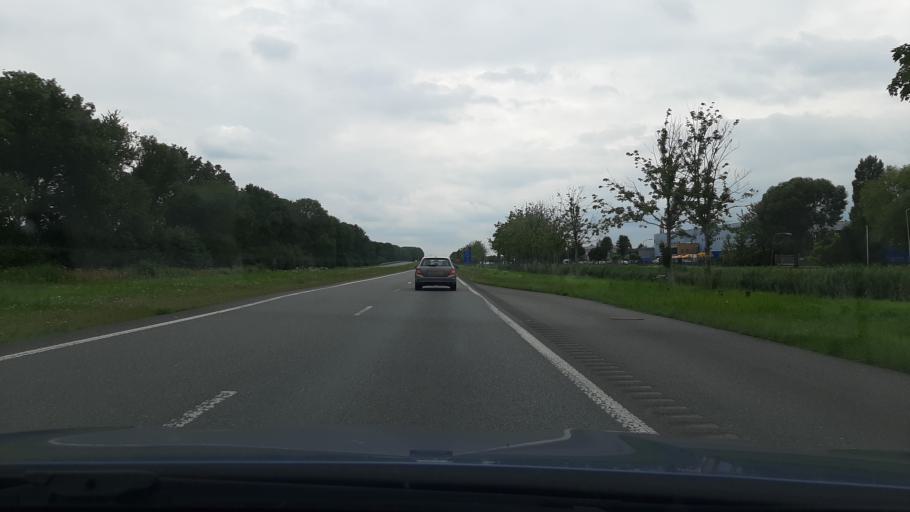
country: NL
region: Flevoland
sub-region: Gemeente Zeewolde
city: Zeewolde
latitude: 52.3547
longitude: 5.5121
